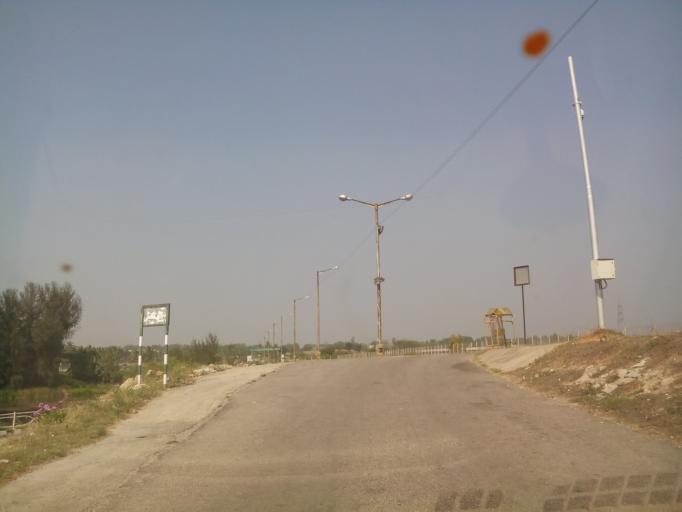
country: IN
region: Karnataka
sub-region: Mandya
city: Shrirangapattana
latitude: 12.4241
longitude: 76.5779
